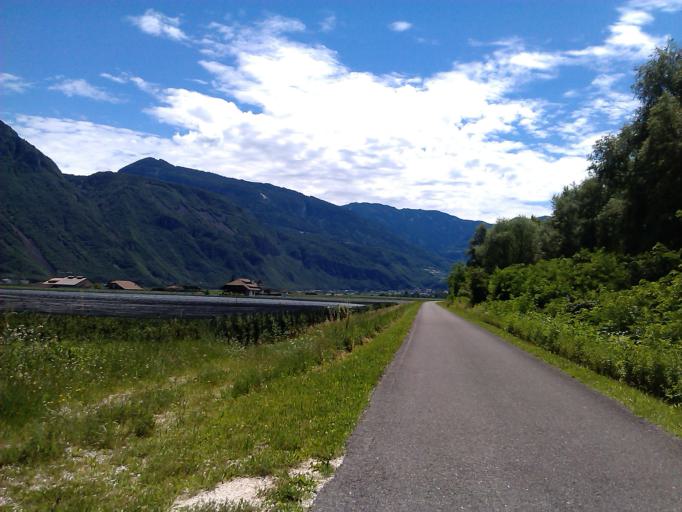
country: IT
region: Trentino-Alto Adige
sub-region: Bolzano
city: Vadena
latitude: 46.3902
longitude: 11.2980
